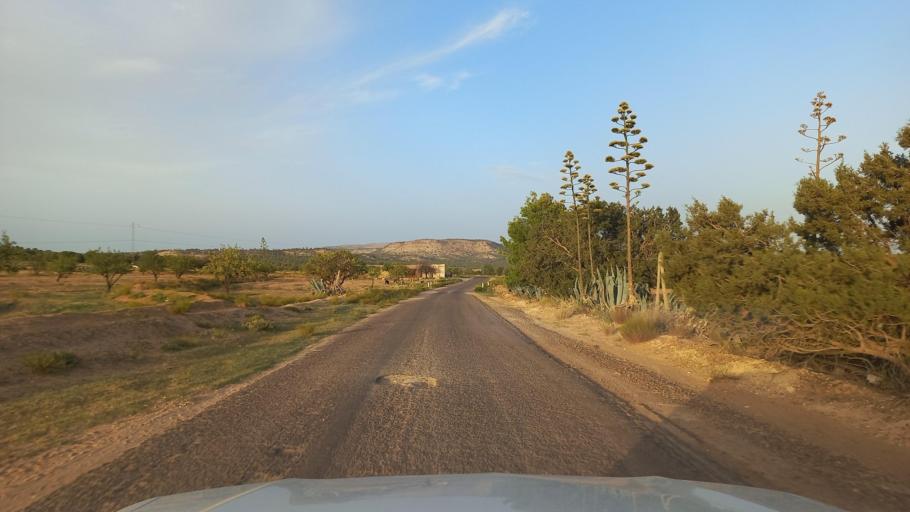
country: TN
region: Al Qasrayn
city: Sbiba
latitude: 35.4077
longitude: 8.9125
